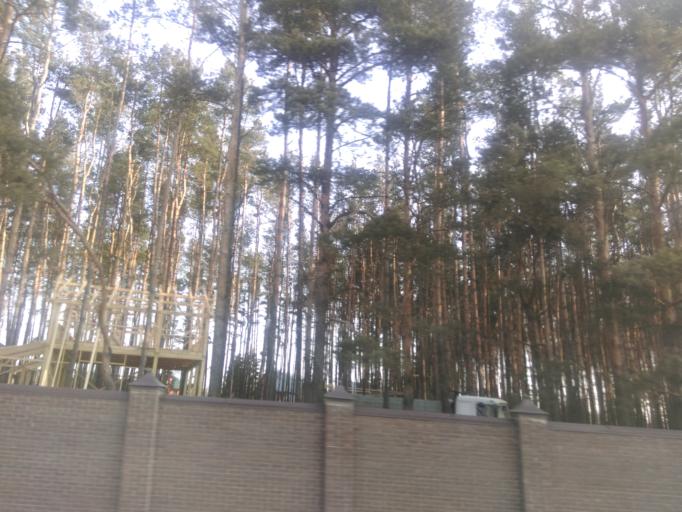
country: RU
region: Moskovskaya
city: Kokoshkino
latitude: 55.5795
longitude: 37.1283
